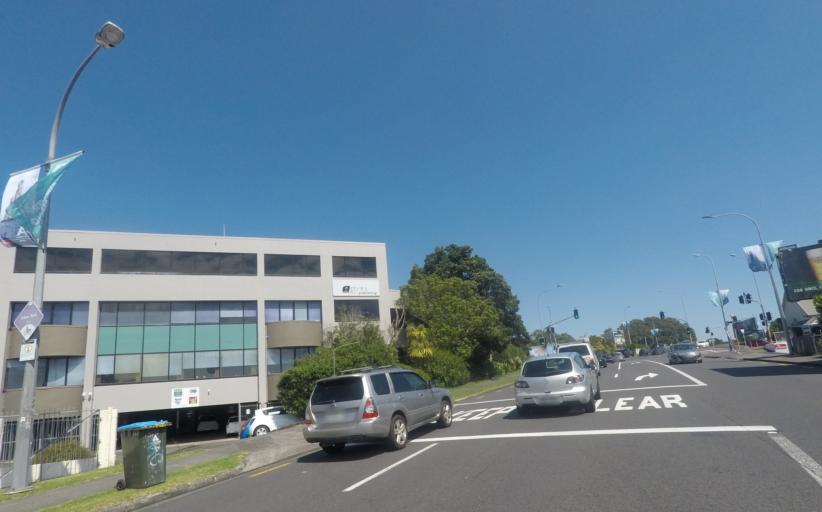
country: NZ
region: Auckland
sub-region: Auckland
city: Auckland
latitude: -36.8709
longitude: 174.7470
